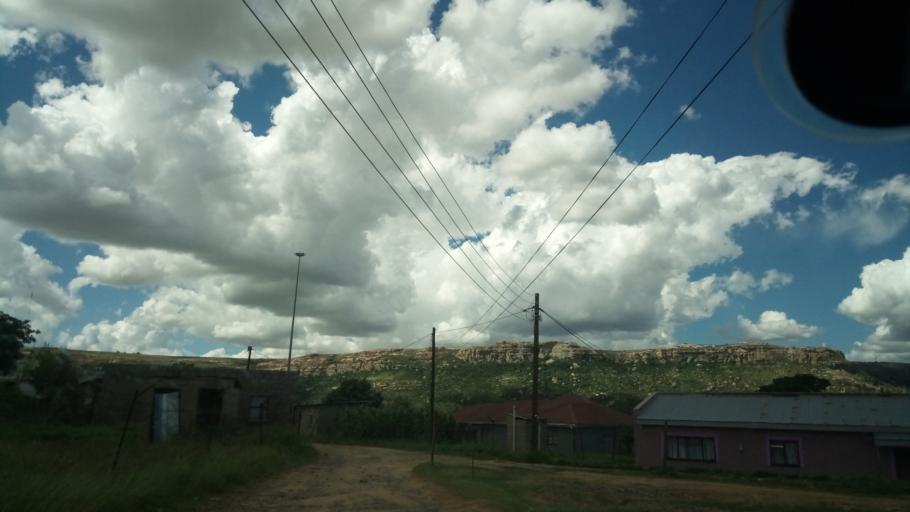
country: LS
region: Maseru
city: Maseru
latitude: -29.3537
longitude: 27.5359
